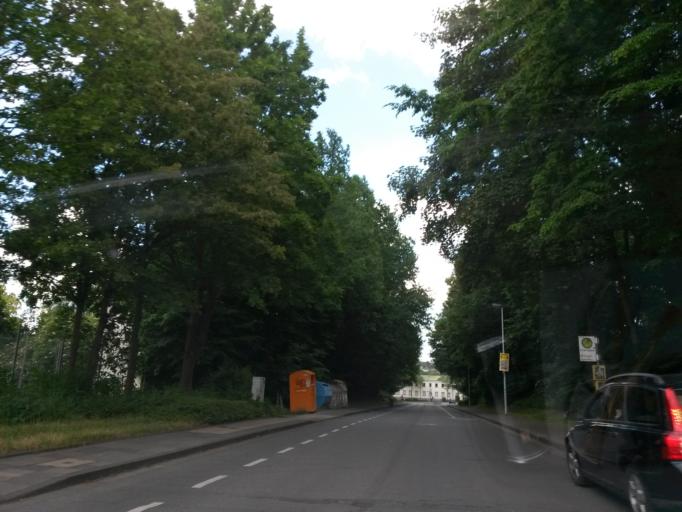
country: DE
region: North Rhine-Westphalia
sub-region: Regierungsbezirk Koln
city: Bonn
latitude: 50.7082
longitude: 7.0650
